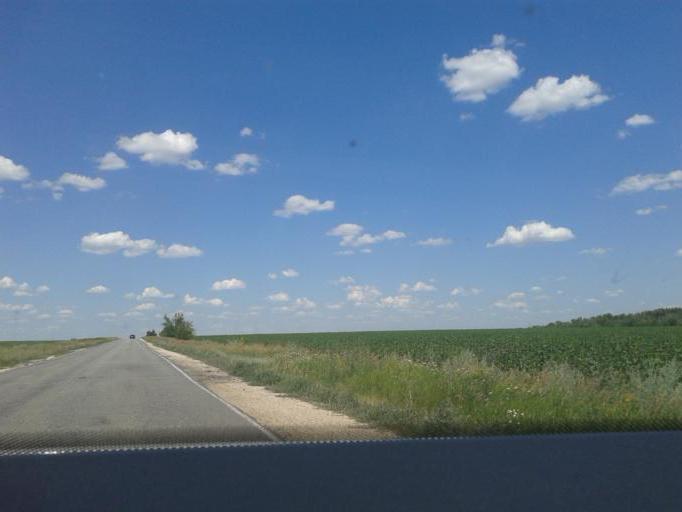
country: RU
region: Volgograd
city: Frolovo
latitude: 49.6523
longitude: 43.6161
